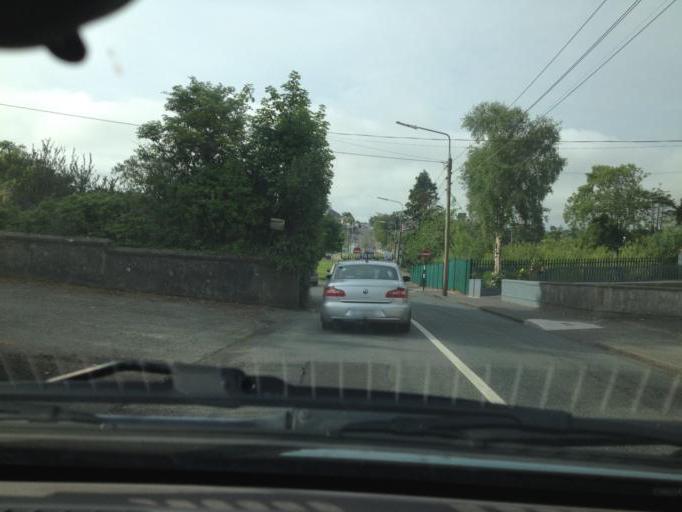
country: IE
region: Connaught
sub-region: Sligo
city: Sligo
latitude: 54.2796
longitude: -8.4751
